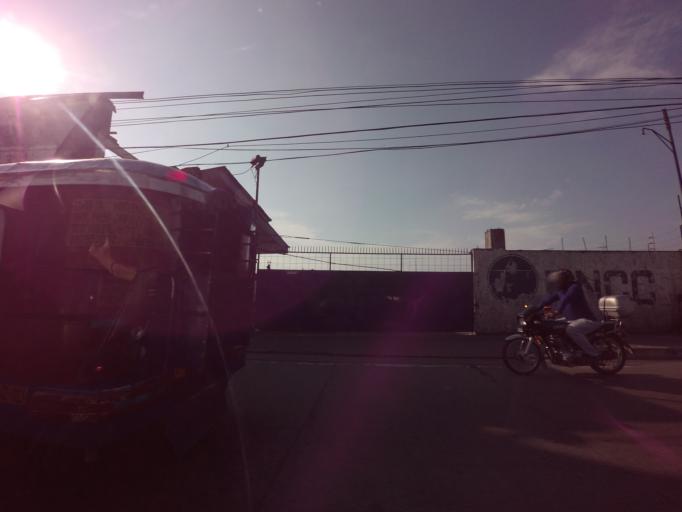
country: PH
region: Calabarzon
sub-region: Province of Rizal
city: Taguig
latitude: 14.4874
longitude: 121.0462
